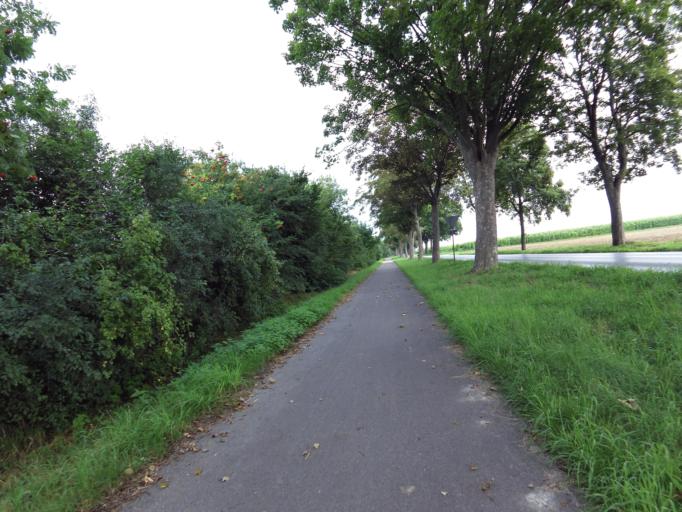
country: DE
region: North Rhine-Westphalia
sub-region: Regierungsbezirk Koln
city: Gangelt
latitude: 50.9884
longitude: 6.0368
